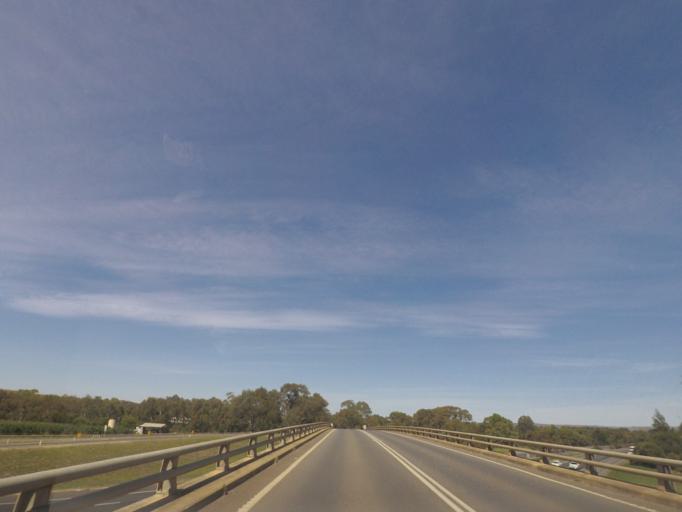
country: AU
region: Victoria
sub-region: Moorabool
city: Bacchus Marsh
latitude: -37.6852
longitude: 144.4817
